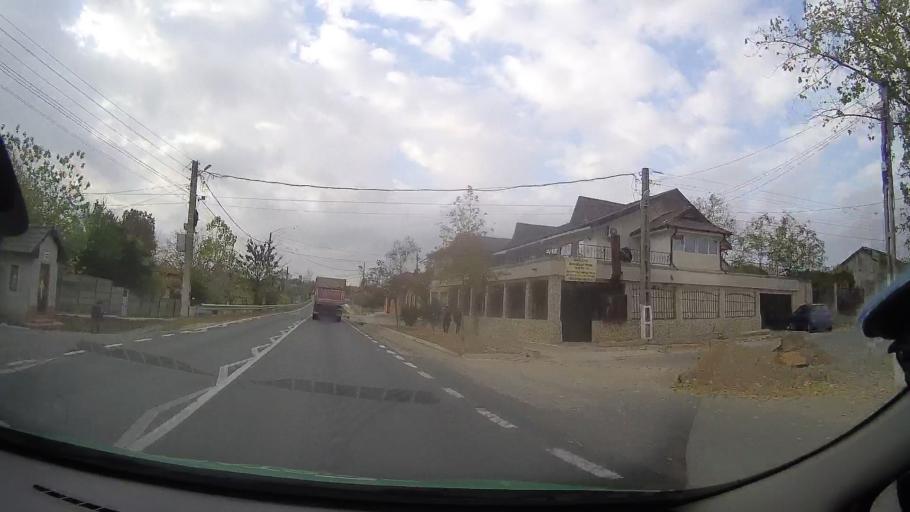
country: RO
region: Constanta
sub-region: Comuna Mircea Voda
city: Satu Nou
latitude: 44.2678
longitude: 28.2256
